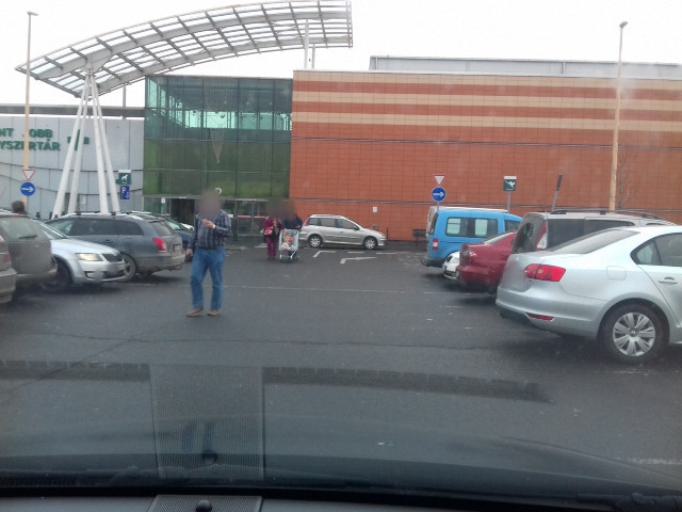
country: HU
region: Pest
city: Dunakeszi
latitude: 47.6066
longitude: 19.1149
